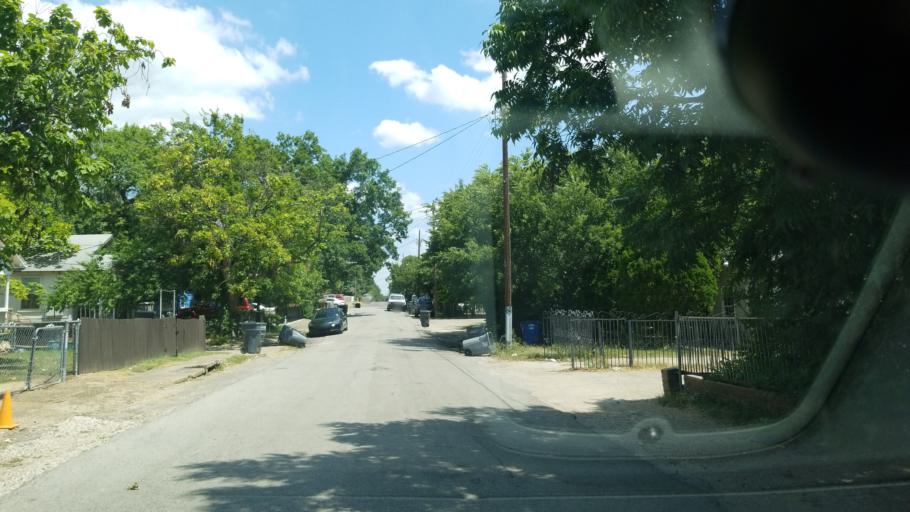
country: US
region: Texas
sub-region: Dallas County
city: Cockrell Hill
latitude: 32.7215
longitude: -96.8390
